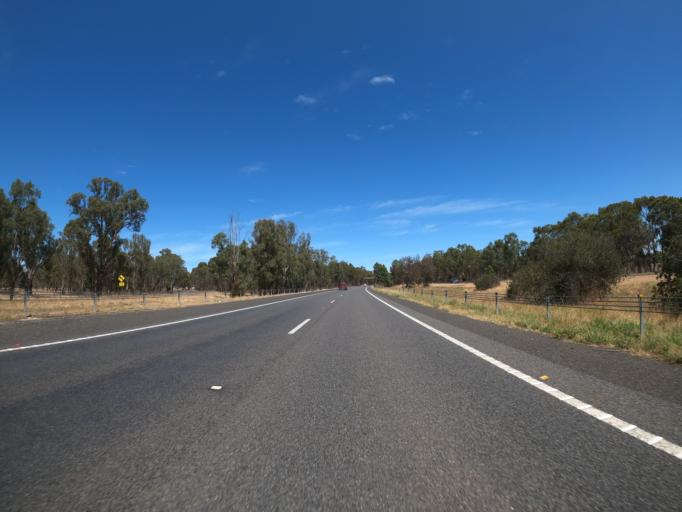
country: AU
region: Victoria
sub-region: Benalla
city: Benalla
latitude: -36.5824
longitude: 145.9637
